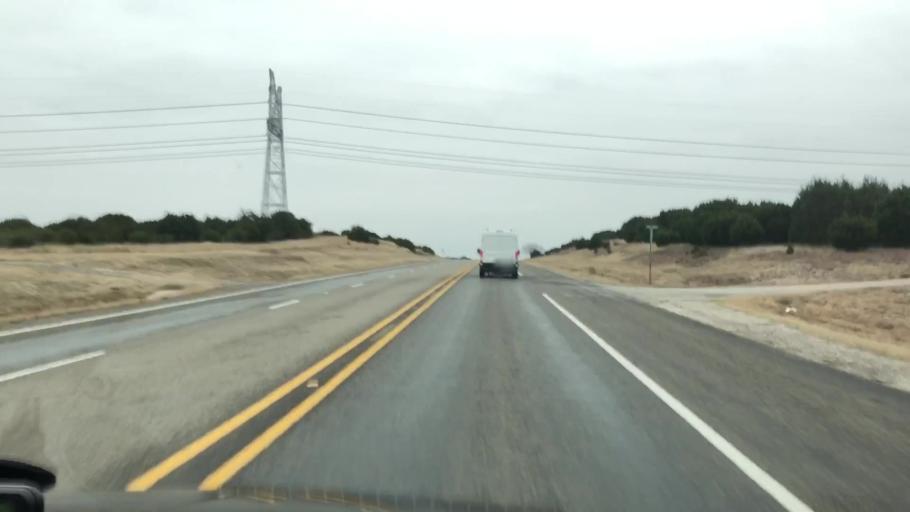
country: US
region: Texas
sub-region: Lampasas County
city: Lampasas
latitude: 31.1427
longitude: -98.1839
